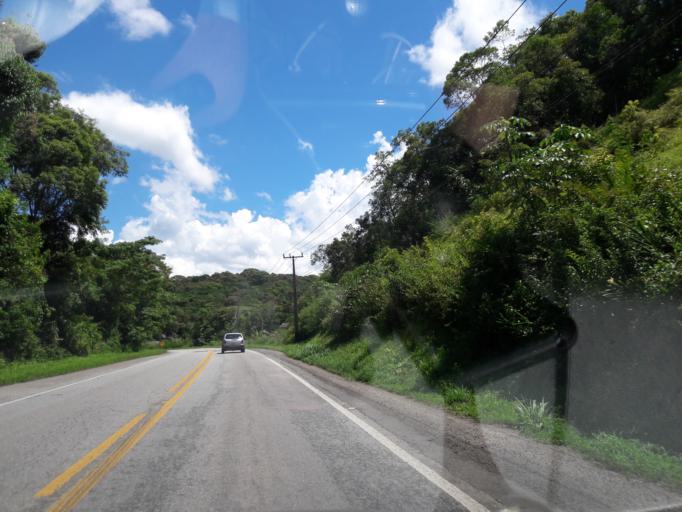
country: BR
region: Parana
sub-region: Antonina
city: Antonina
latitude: -25.4507
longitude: -48.8047
